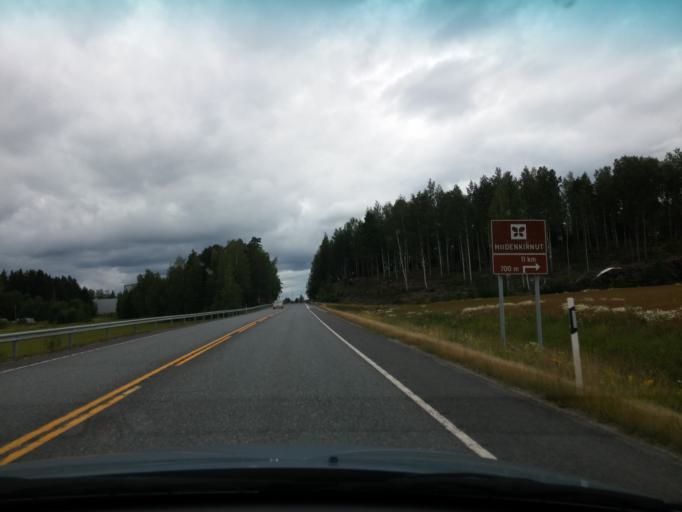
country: FI
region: Uusimaa
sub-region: Porvoo
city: Askola
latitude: 60.4896
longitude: 25.5567
